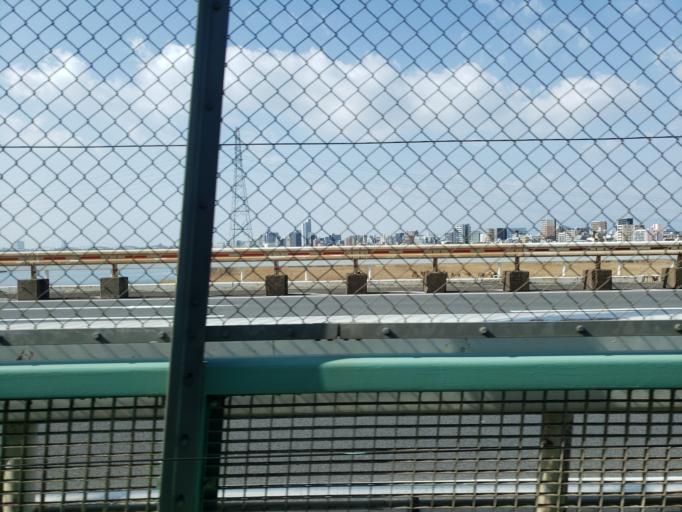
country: JP
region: Osaka
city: Osaka-shi
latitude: 34.7201
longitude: 135.4993
